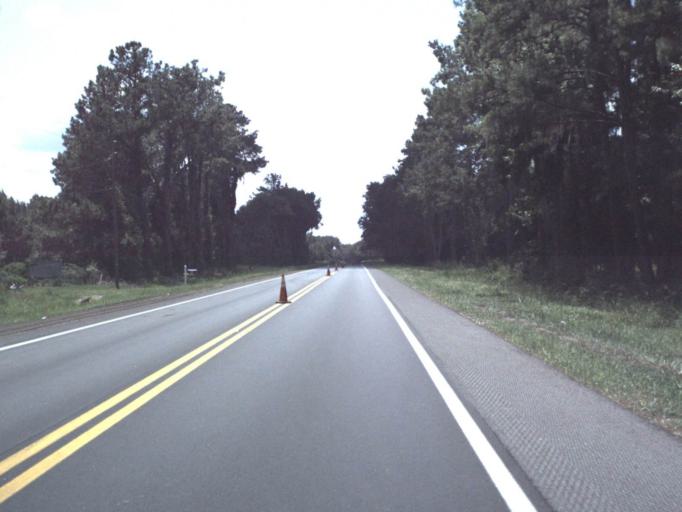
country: US
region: Florida
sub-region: Alachua County
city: Alachua
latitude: 29.7963
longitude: -82.3833
